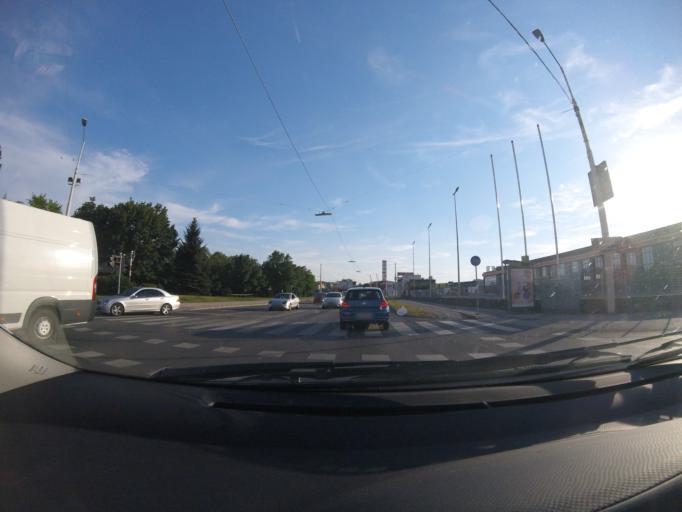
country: AT
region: Lower Austria
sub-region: Wiener Neustadt Stadt
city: Wiener Neustadt
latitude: 47.8262
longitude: 16.2519
